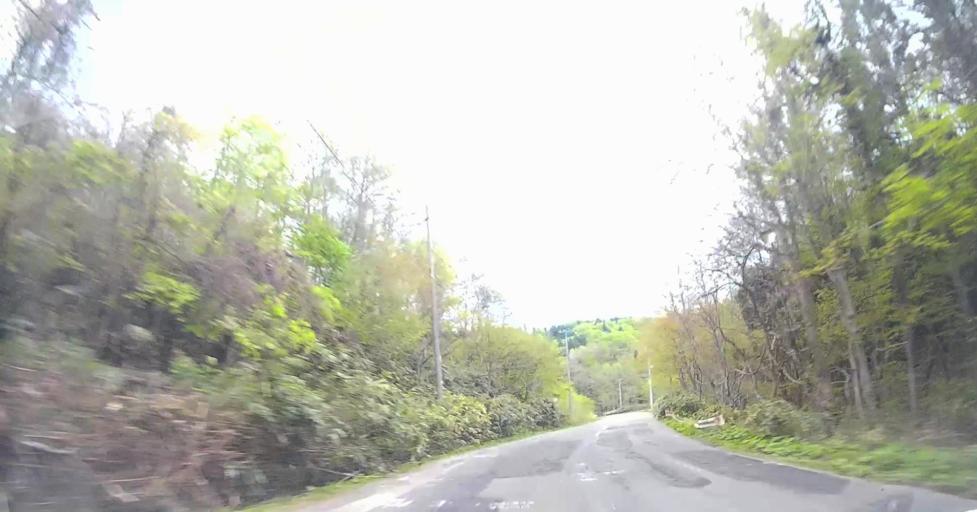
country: JP
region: Aomori
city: Goshogawara
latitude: 41.1153
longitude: 140.5285
